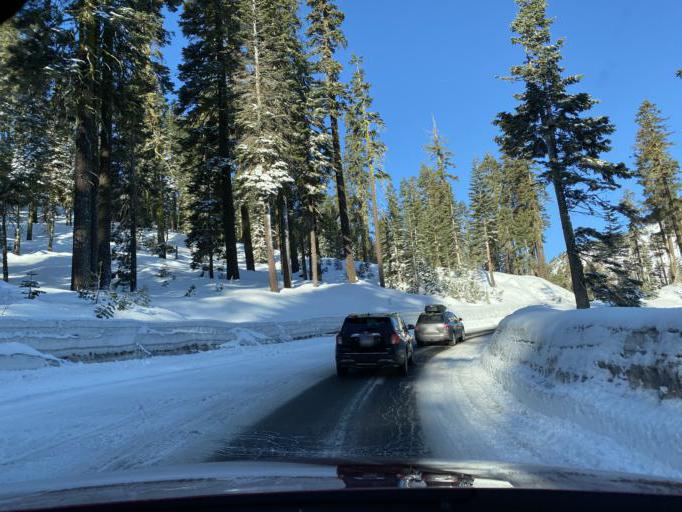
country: US
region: California
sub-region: El Dorado County
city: South Lake Tahoe
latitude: 38.8069
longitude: -120.0815
